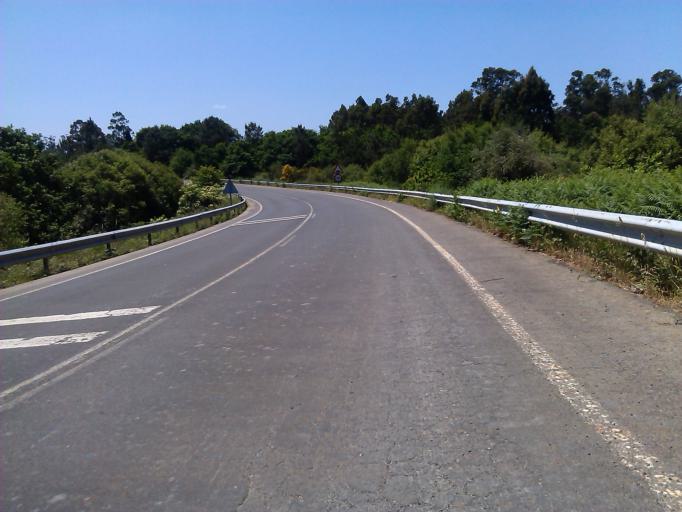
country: ES
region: Galicia
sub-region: Provincia da Coruna
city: Oroso
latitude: 42.9131
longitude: -8.4233
